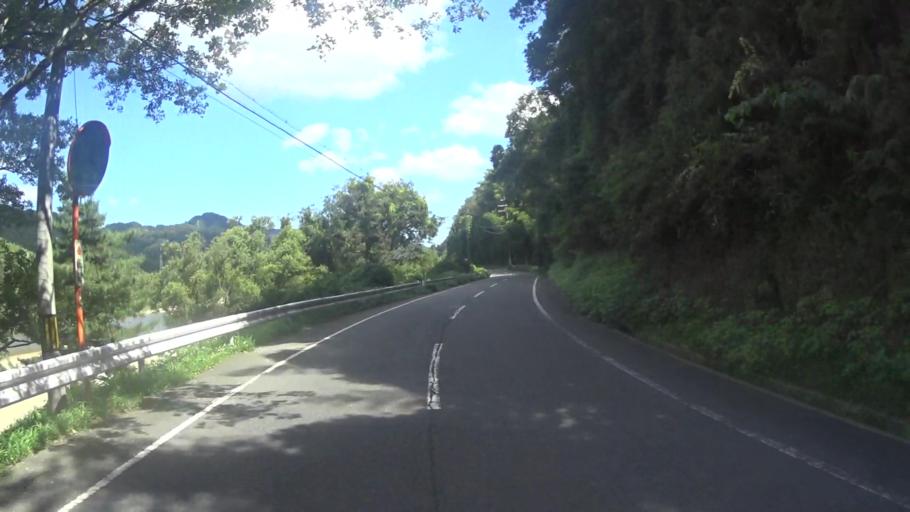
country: JP
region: Nara
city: Nara-shi
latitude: 34.7505
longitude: 135.8368
